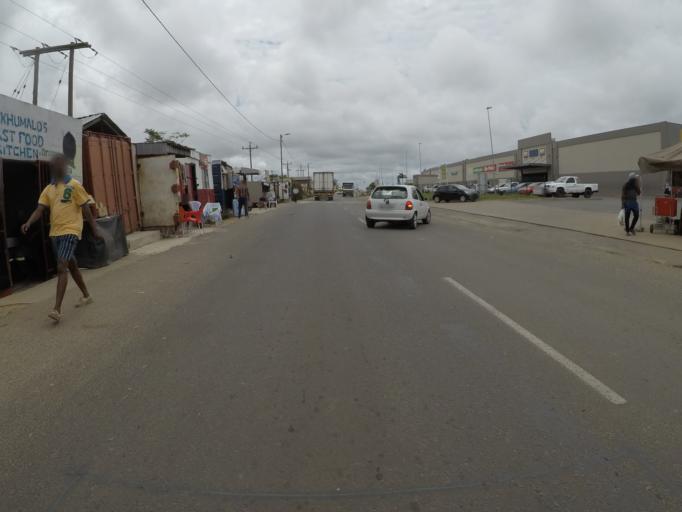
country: ZA
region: KwaZulu-Natal
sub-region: uThungulu District Municipality
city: eSikhawini
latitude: -28.8726
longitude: 31.8984
